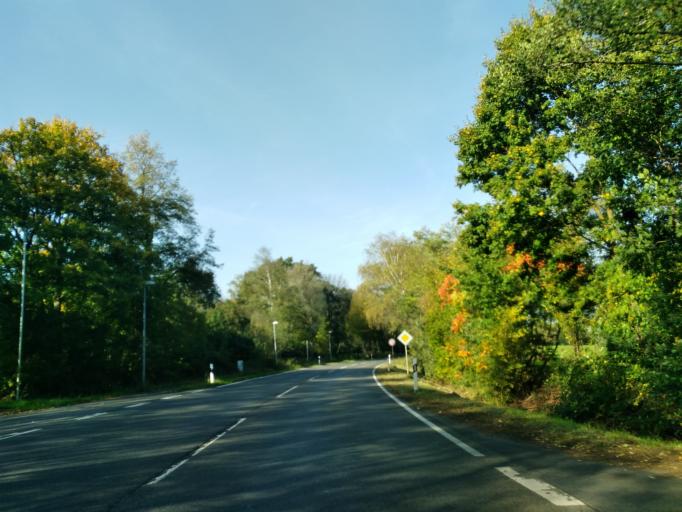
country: DE
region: North Rhine-Westphalia
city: Sankt Augustin
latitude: 50.7564
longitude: 7.2145
